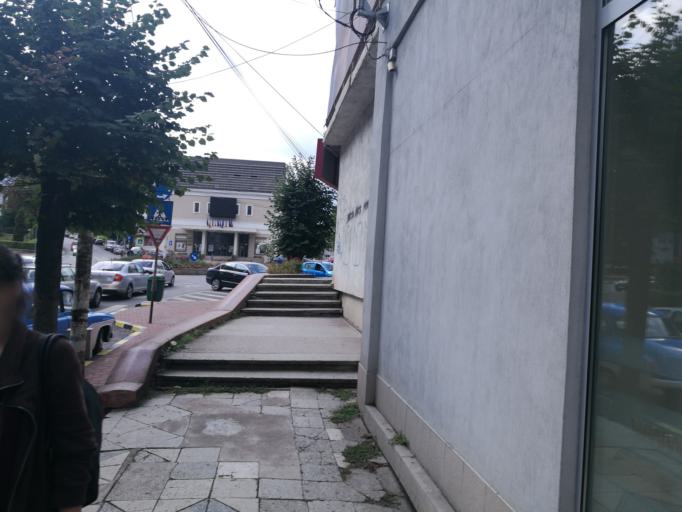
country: RO
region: Suceava
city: Suceava
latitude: 47.6460
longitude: 26.2578
